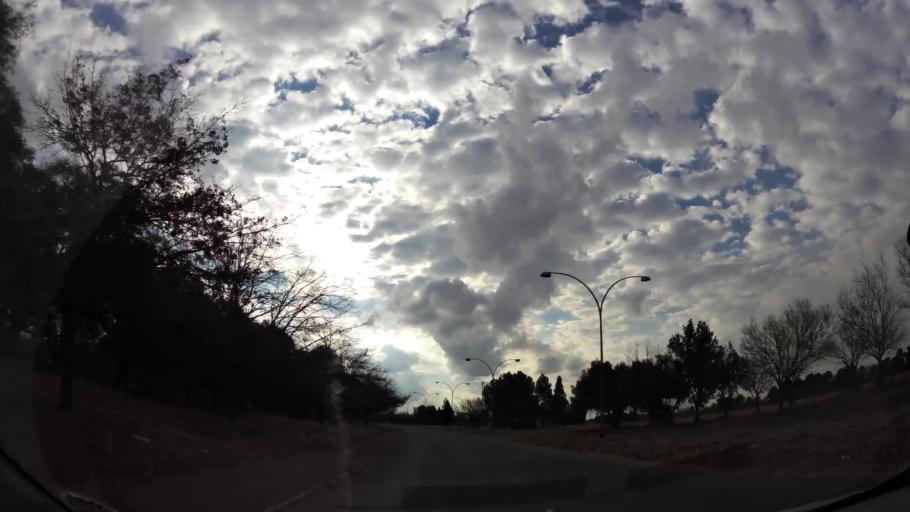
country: ZA
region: Orange Free State
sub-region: Fezile Dabi District Municipality
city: Sasolburg
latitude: -26.7990
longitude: 27.8282
